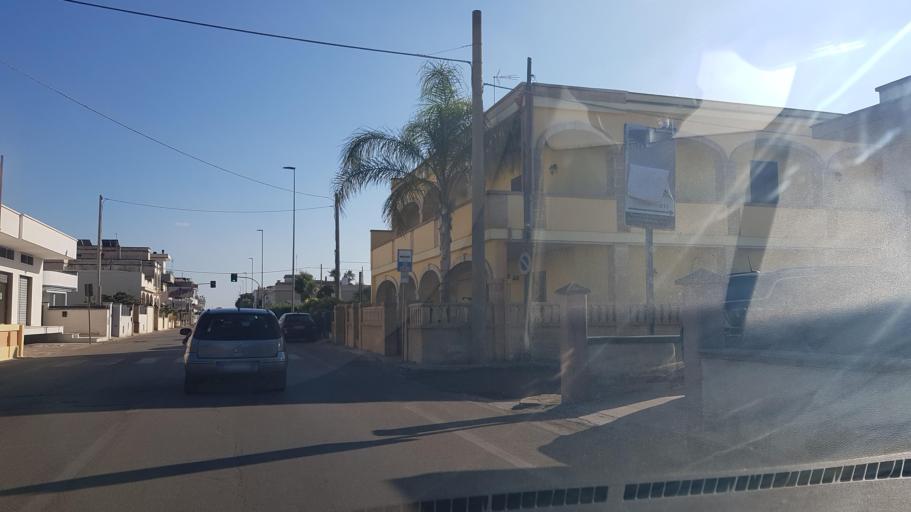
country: IT
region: Apulia
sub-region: Provincia di Lecce
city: Montesano Salentino
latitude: 39.9780
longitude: 18.3246
